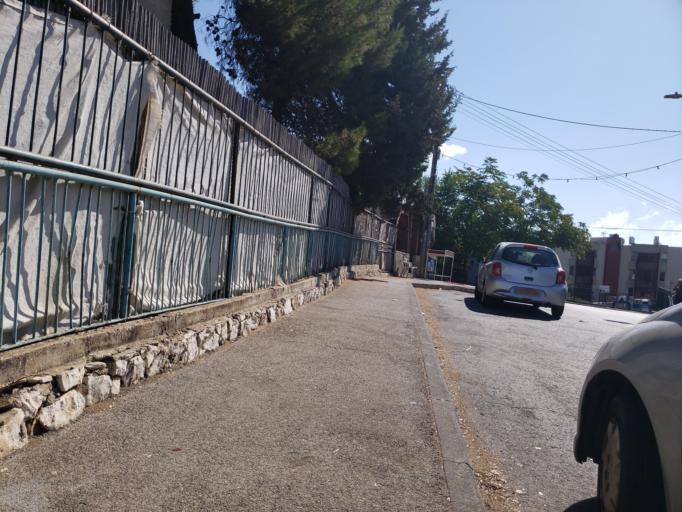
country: IL
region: Northern District
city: Safed
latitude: 32.9587
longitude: 35.4994
